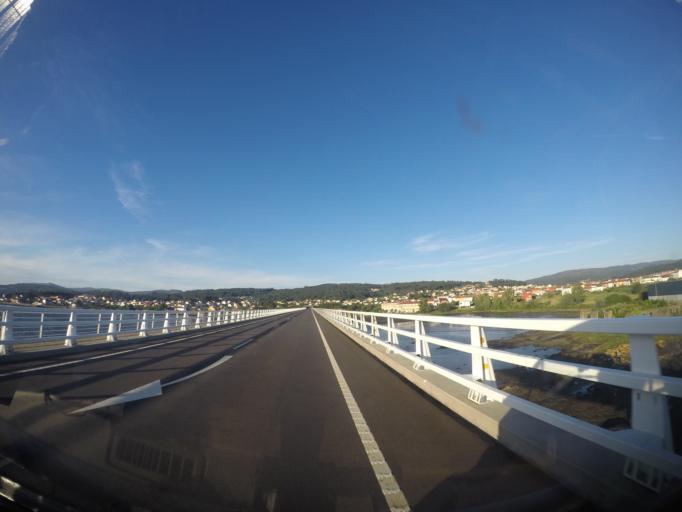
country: ES
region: Galicia
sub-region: Provincia da Coruna
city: Noia
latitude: 42.7943
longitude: -8.8984
